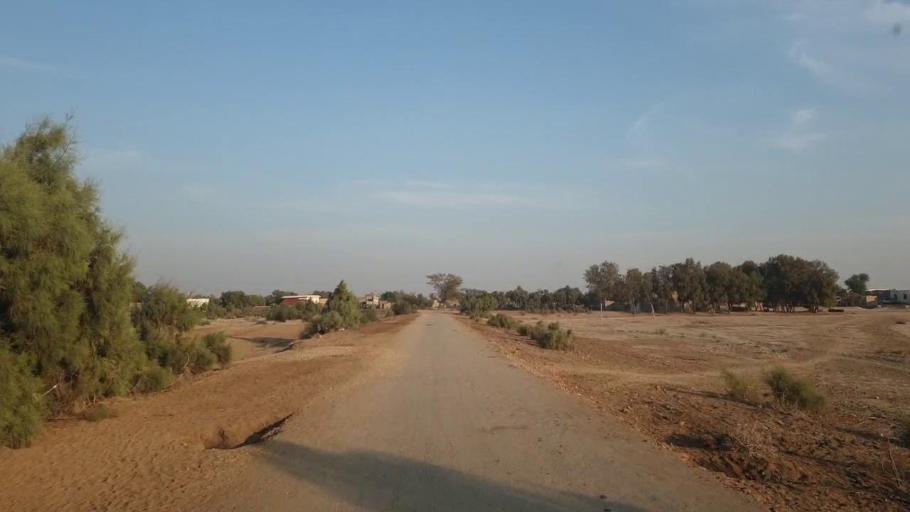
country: PK
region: Sindh
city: Sann
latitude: 25.9223
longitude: 68.1901
